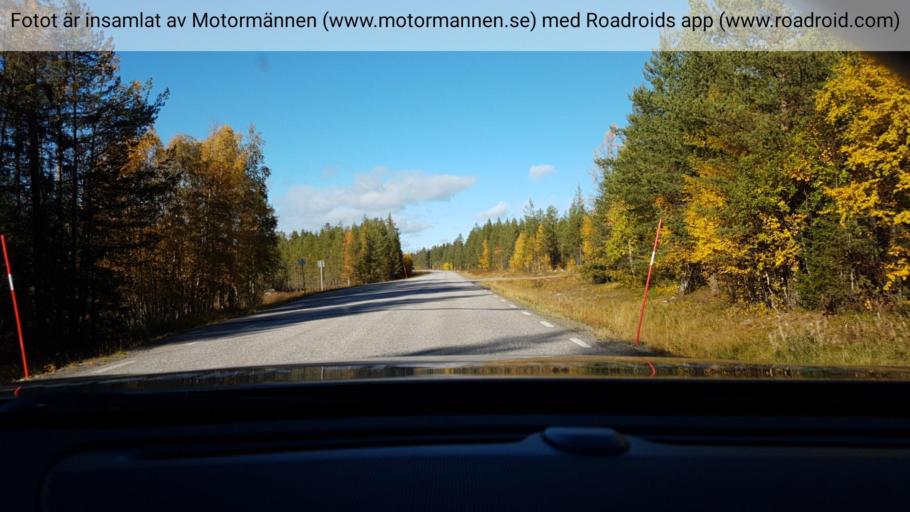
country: SE
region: Norrbotten
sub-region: Arvidsjaurs Kommun
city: Arvidsjaur
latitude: 65.6780
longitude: 18.8275
